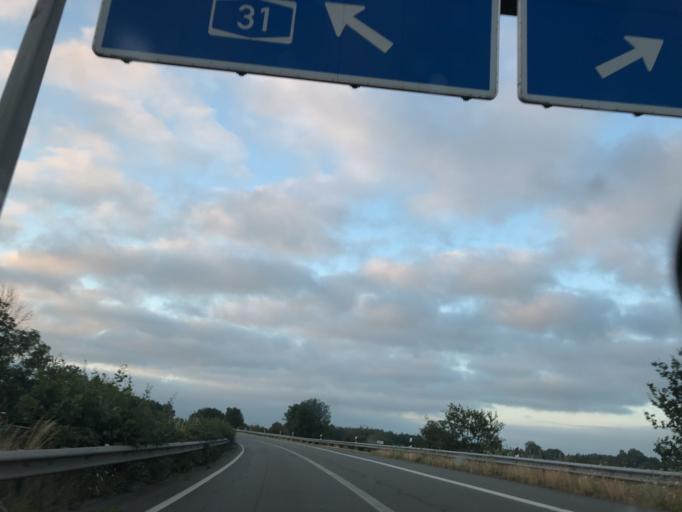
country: DE
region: Lower Saxony
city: Bunde
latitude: 53.1643
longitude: 7.2776
